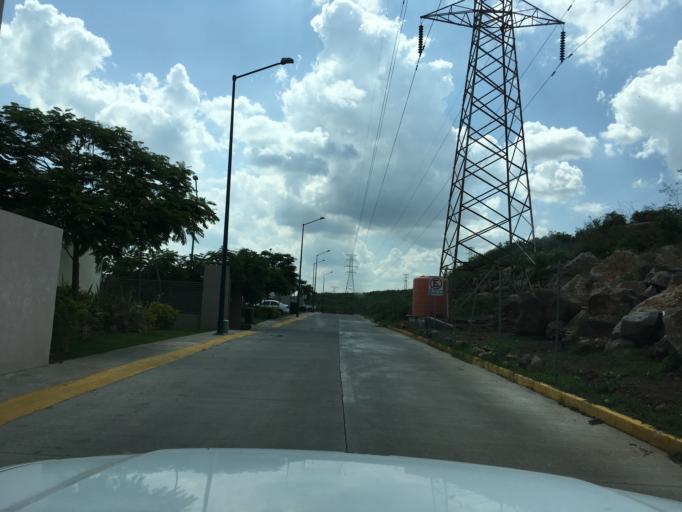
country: MX
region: Jalisco
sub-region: Tlajomulco de Zuniga
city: Altus Bosques
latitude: 20.5866
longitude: -103.3662
